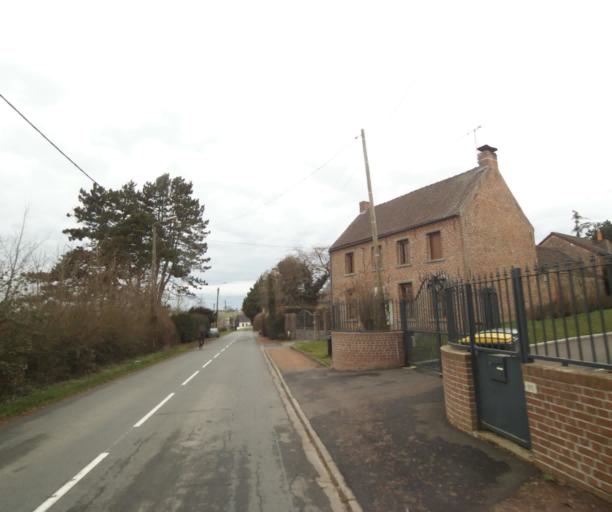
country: FR
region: Nord-Pas-de-Calais
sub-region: Departement du Nord
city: Sebourg
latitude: 50.3333
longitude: 3.6554
